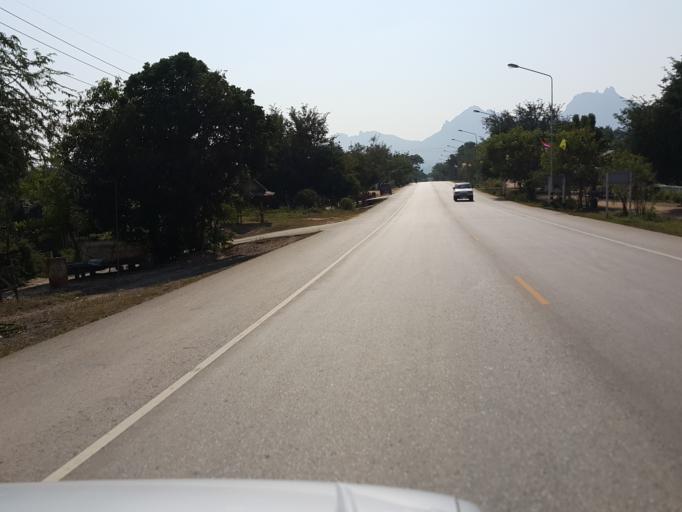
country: TH
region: Lampang
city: Chae Hom
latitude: 18.7742
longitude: 99.5755
